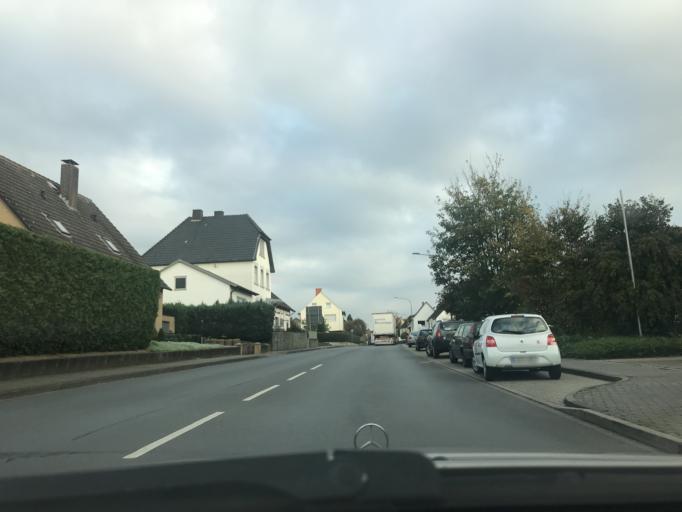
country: DE
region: North Rhine-Westphalia
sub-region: Regierungsbezirk Arnsberg
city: Soest
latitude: 51.6349
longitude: 8.0986
